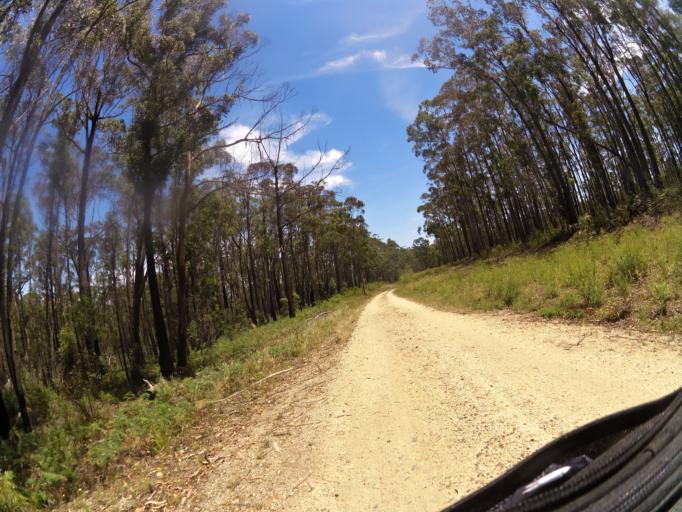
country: AU
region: Victoria
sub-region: East Gippsland
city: Lakes Entrance
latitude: -37.7595
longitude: 147.9393
